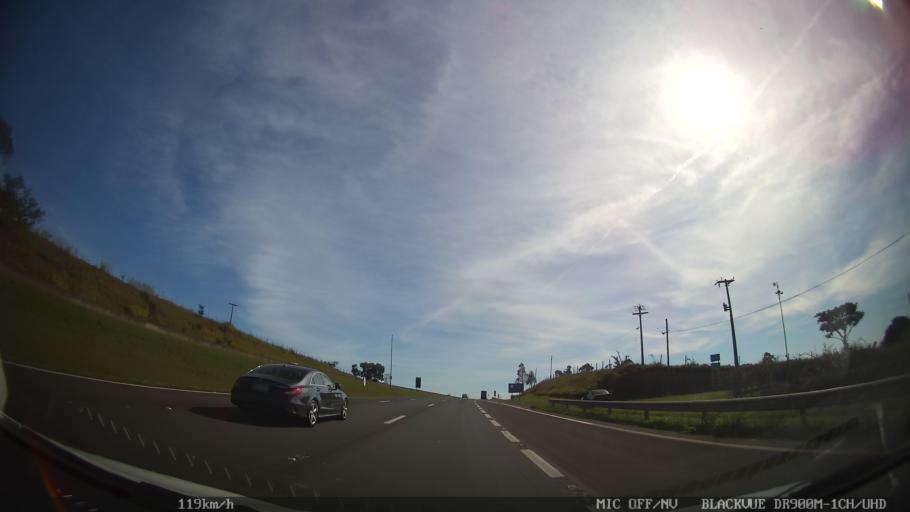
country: BR
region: Sao Paulo
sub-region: Araras
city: Araras
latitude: -22.3884
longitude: -47.3938
